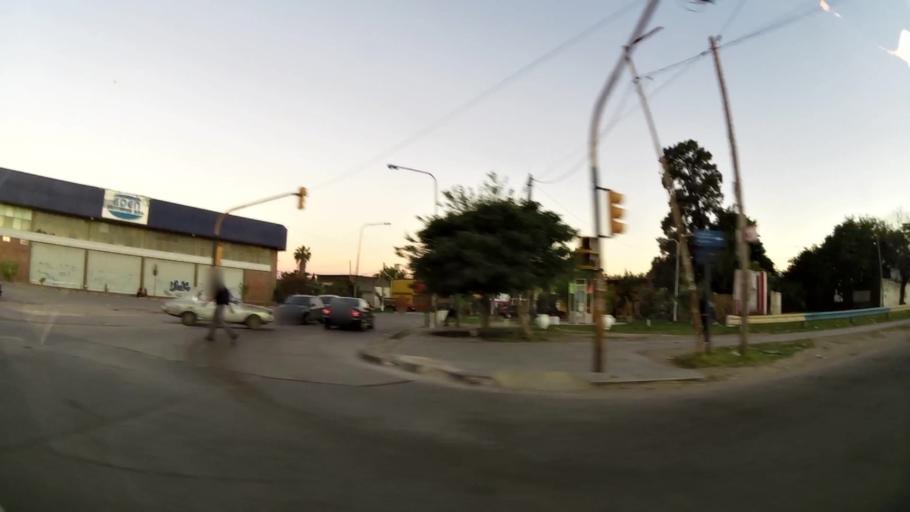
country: AR
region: Buenos Aires
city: San Justo
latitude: -34.7250
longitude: -58.5982
